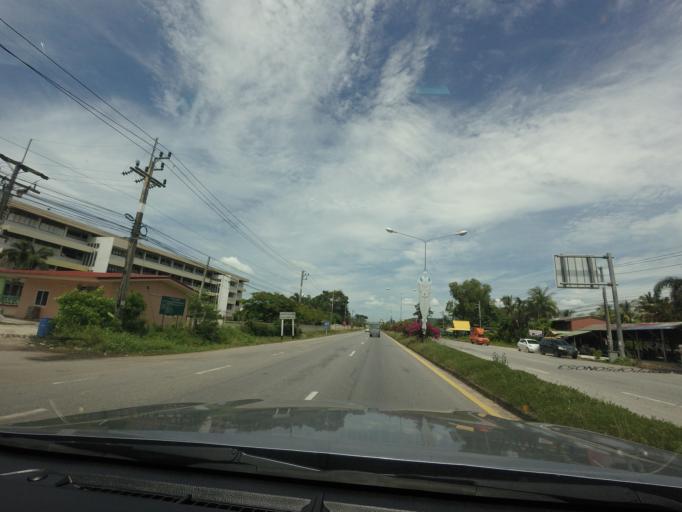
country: TH
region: Songkhla
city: Singhanakhon
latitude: 7.2417
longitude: 100.5459
